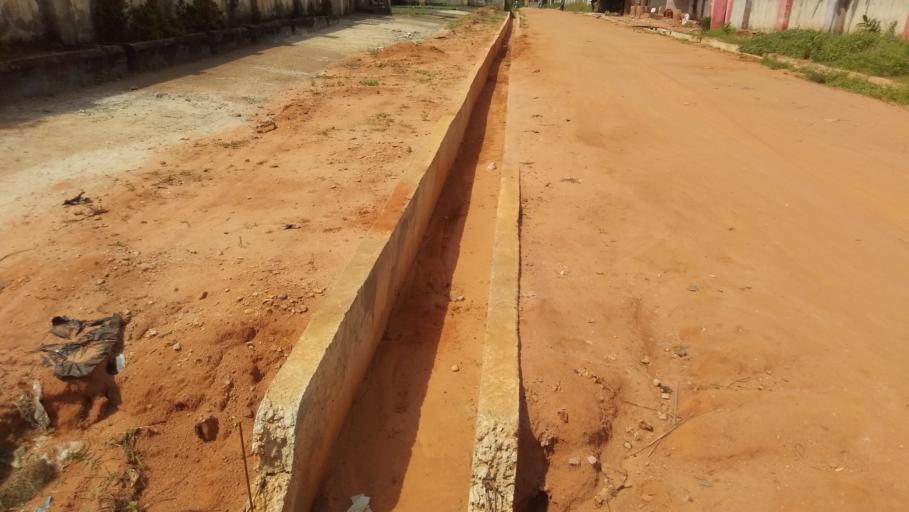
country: NG
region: Imo
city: Orodo
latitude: 5.5746
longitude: 6.9450
